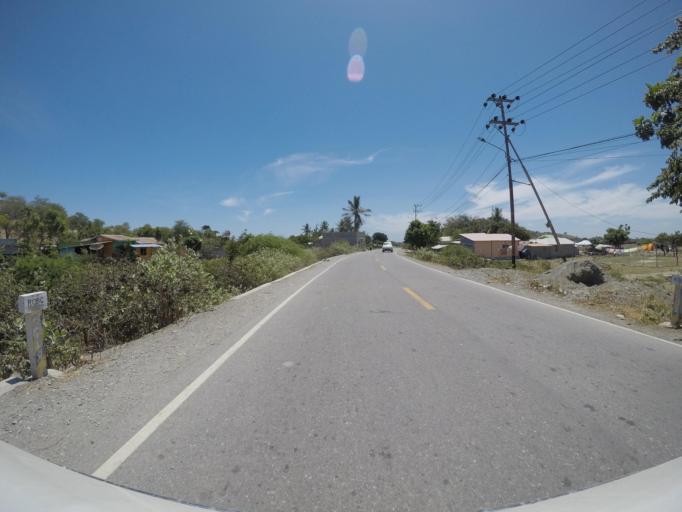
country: TL
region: Manatuto
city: Manatuto
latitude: -8.5230
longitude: 126.0062
